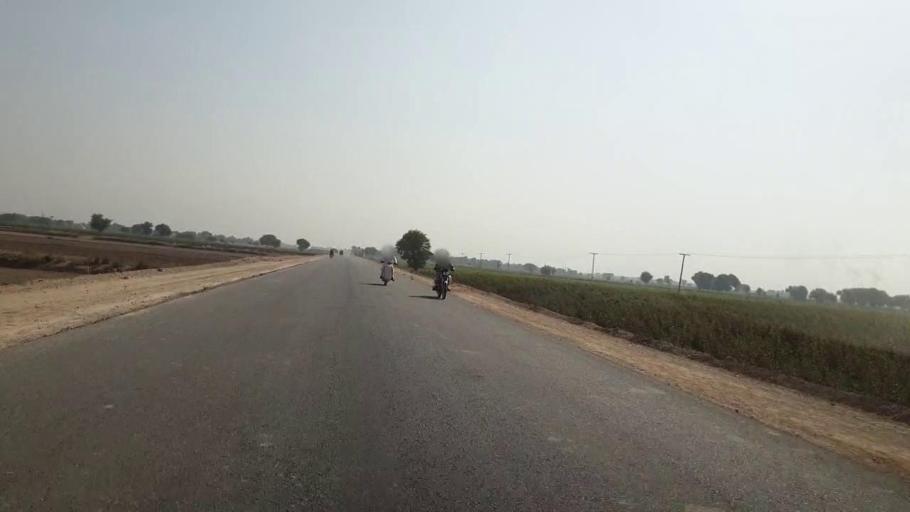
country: PK
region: Sindh
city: Dadu
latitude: 26.6588
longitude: 67.7762
